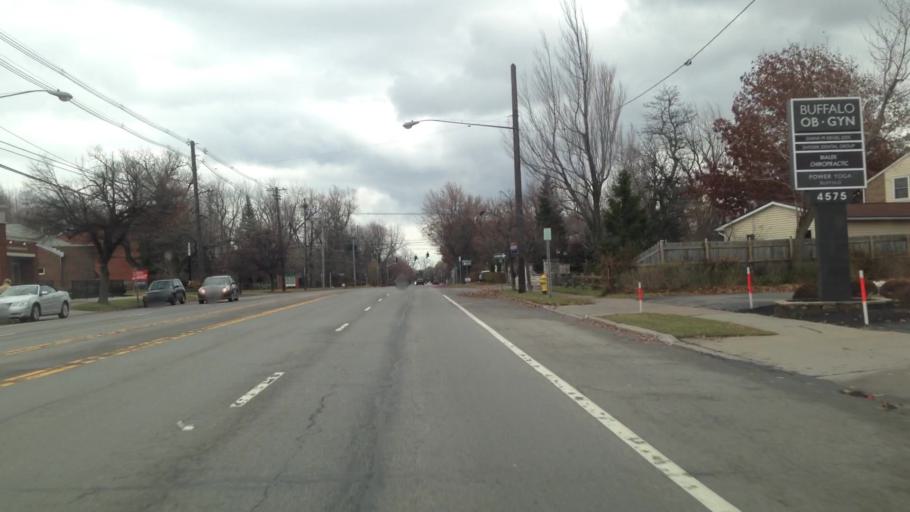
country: US
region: New York
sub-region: Erie County
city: Eggertsville
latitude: 42.9624
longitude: -78.7809
